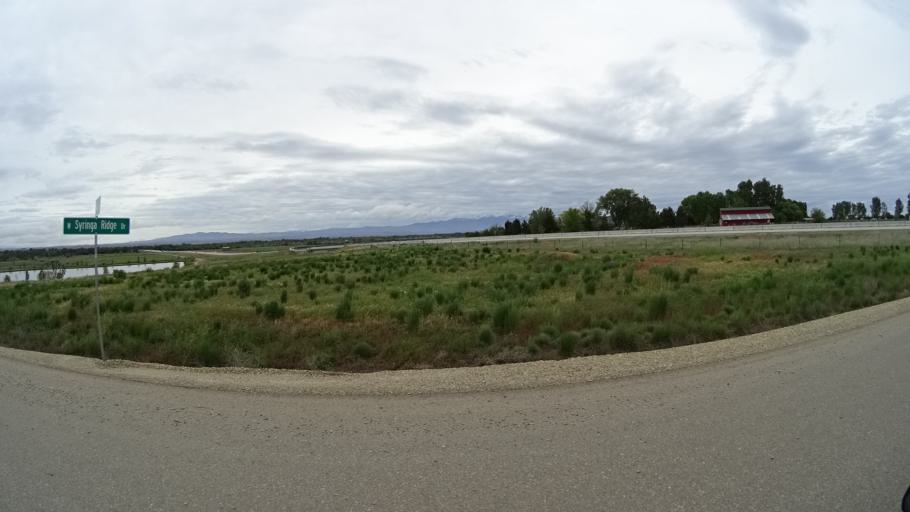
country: US
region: Idaho
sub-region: Ada County
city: Star
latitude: 43.6689
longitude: -116.4698
